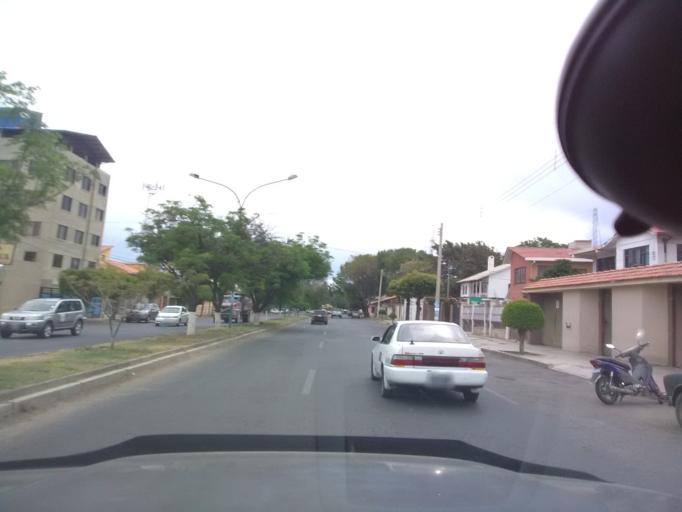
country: BO
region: Cochabamba
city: Cochabamba
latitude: -17.3825
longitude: -66.1670
